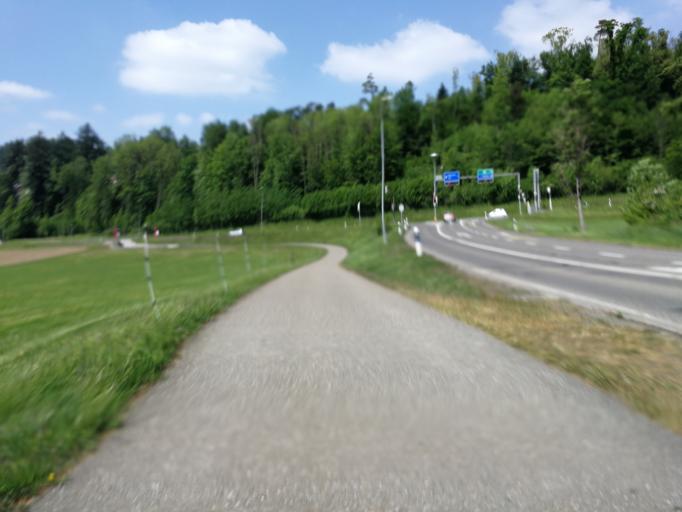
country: CH
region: Saint Gallen
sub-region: Wahlkreis See-Gaster
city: Jona
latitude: 47.2287
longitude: 8.8589
